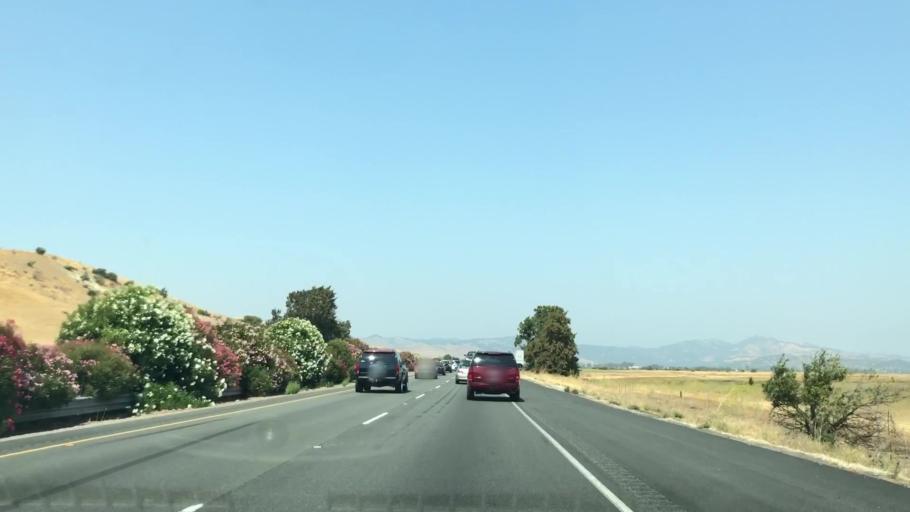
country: US
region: California
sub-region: Solano County
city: Green Valley
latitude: 38.1573
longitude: -122.1168
